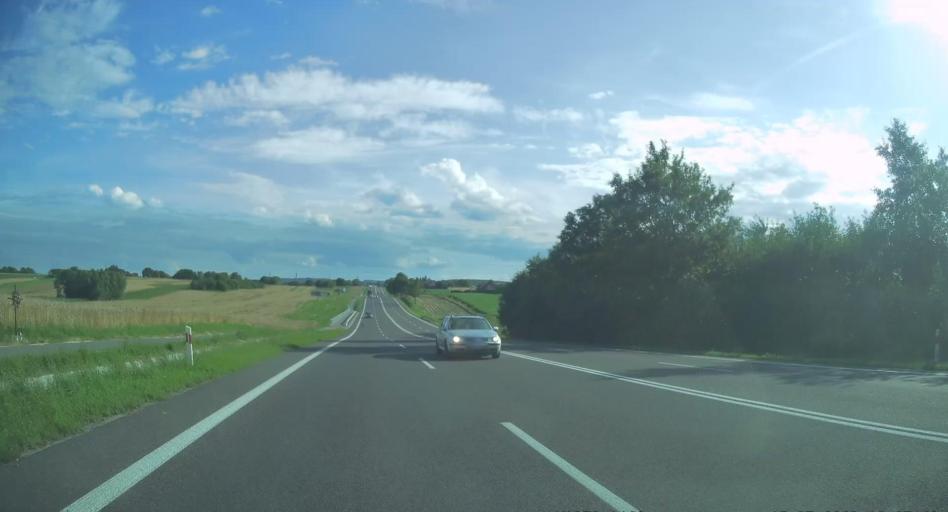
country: PL
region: Subcarpathian Voivodeship
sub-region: Powiat przemyski
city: Zurawica
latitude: 49.8330
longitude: 22.7949
